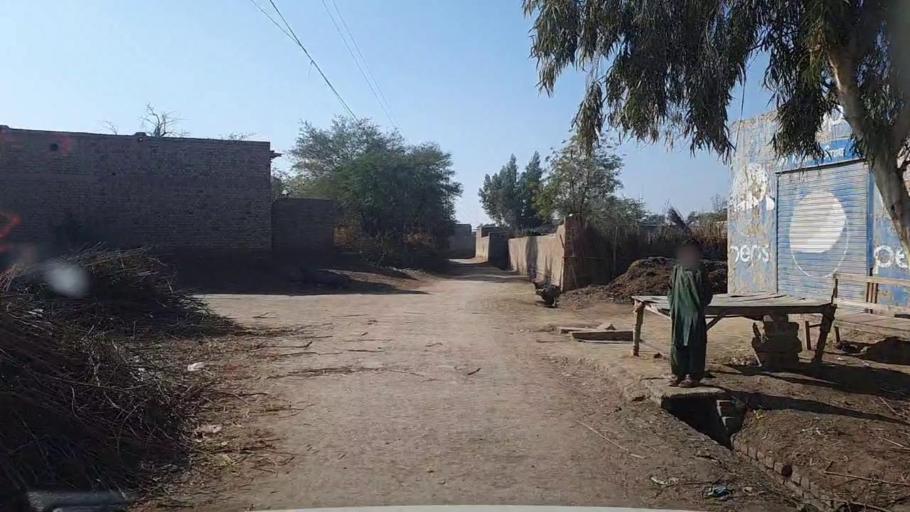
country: PK
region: Sindh
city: Khairpur
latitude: 27.9560
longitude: 69.6858
